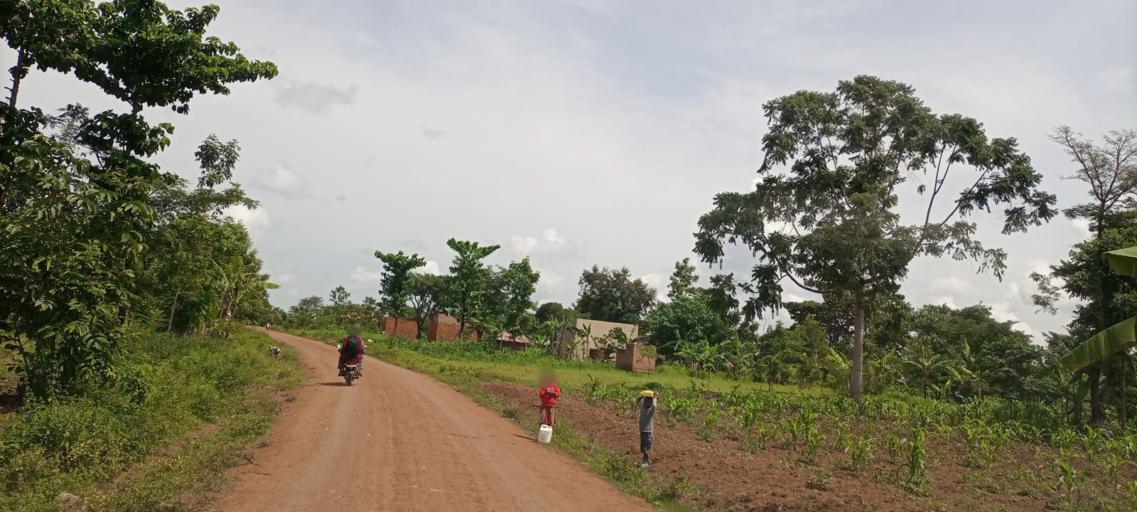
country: UG
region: Eastern Region
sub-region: Budaka District
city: Budaka
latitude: 1.1706
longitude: 33.9387
